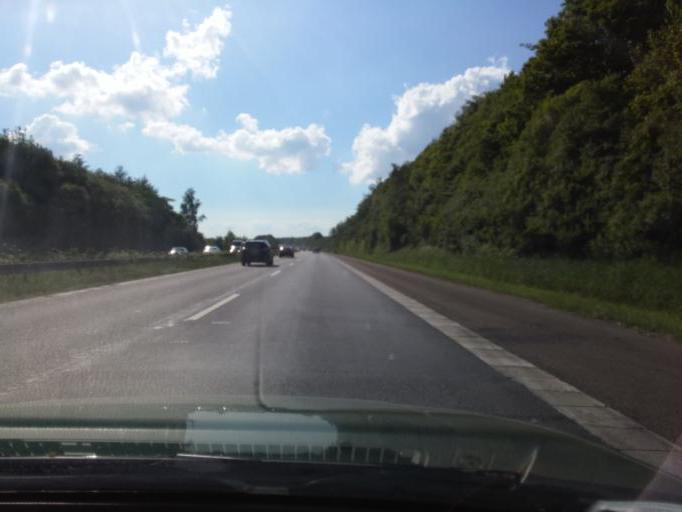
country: DK
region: South Denmark
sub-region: Assens Kommune
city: Vissenbjerg
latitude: 55.4083
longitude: 10.1247
